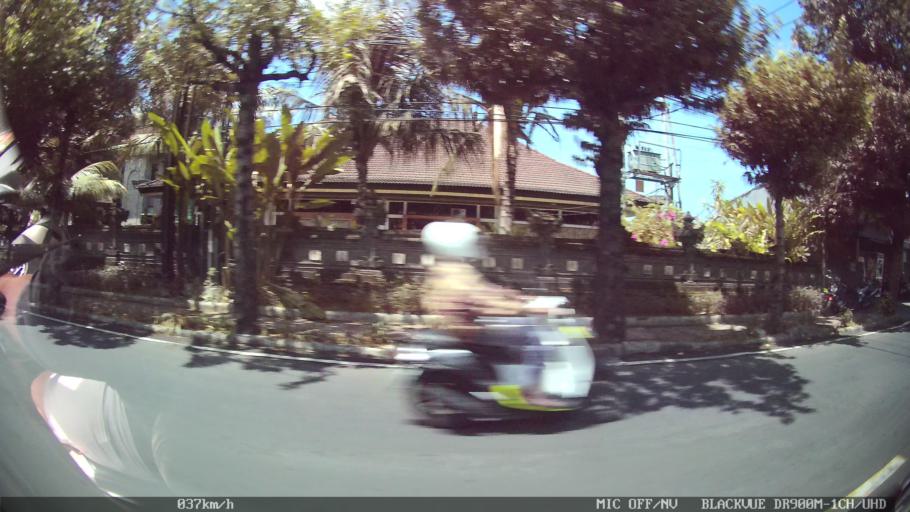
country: ID
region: Bali
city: Banjar Jabejero
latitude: -8.6016
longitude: 115.2650
